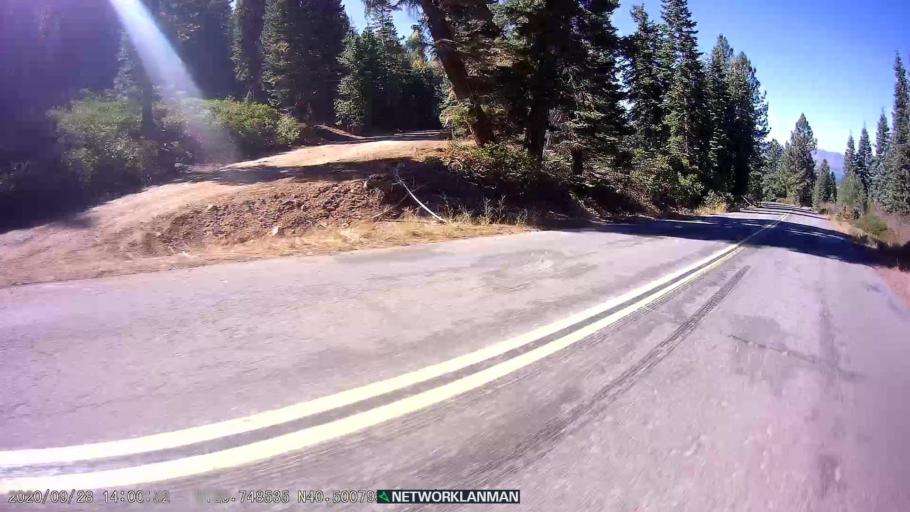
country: US
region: California
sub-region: Lassen County
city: Susanville
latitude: 40.5011
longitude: -120.7489
